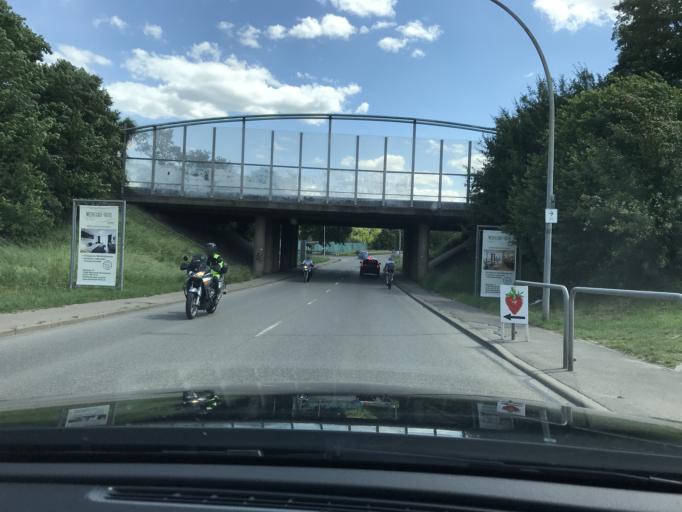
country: DE
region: Baden-Wuerttemberg
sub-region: Regierungsbezirk Stuttgart
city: Weinstadt-Endersbach
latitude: 48.8162
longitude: 9.3890
